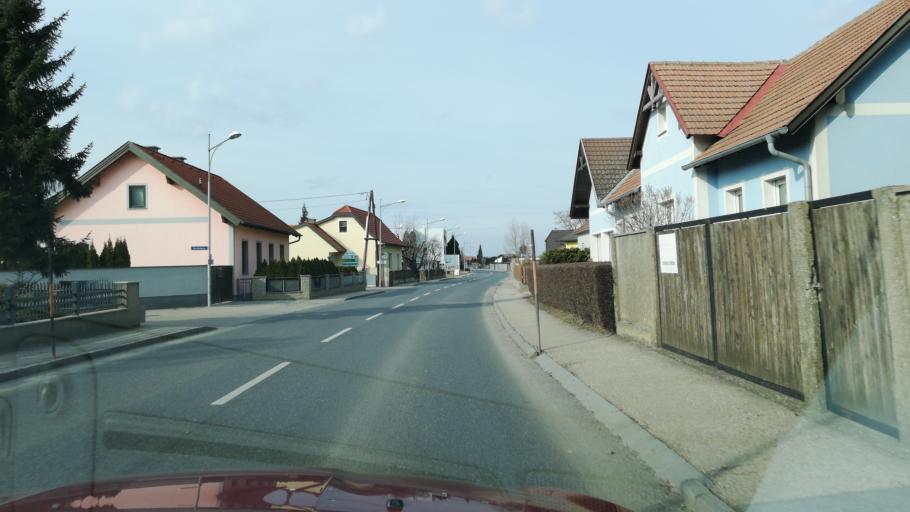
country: AT
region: Lower Austria
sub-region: Politischer Bezirk Tulln
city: Atzenbrugg
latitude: 48.3023
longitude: 15.8926
